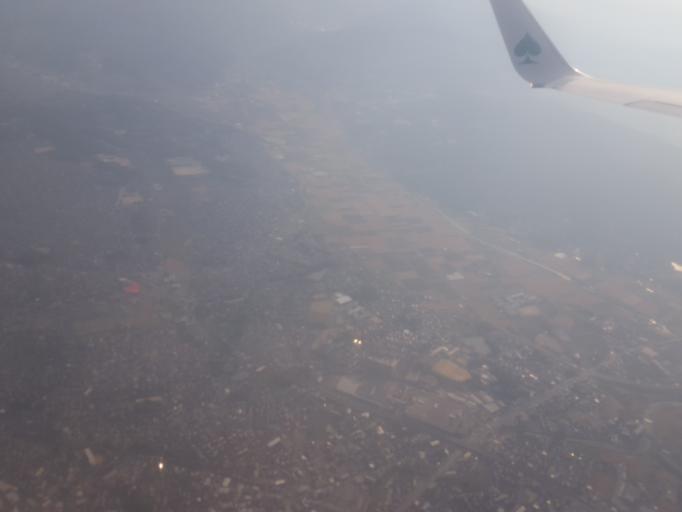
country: JP
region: Fukuoka
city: Chikushino-shi
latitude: 33.4783
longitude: 130.5207
